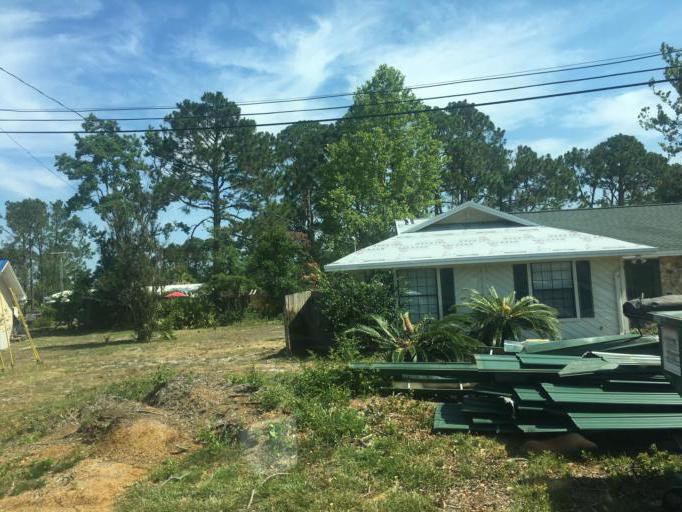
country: US
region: Florida
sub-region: Bay County
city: Upper Grand Lagoon
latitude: 30.1647
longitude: -85.7622
